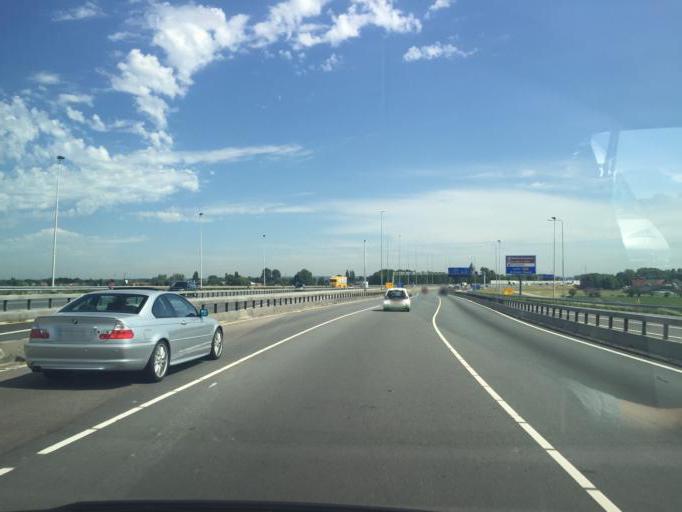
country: NL
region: Gelderland
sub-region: Gemeente Overbetuwe
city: Herveld
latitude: 51.8921
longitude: 5.7406
